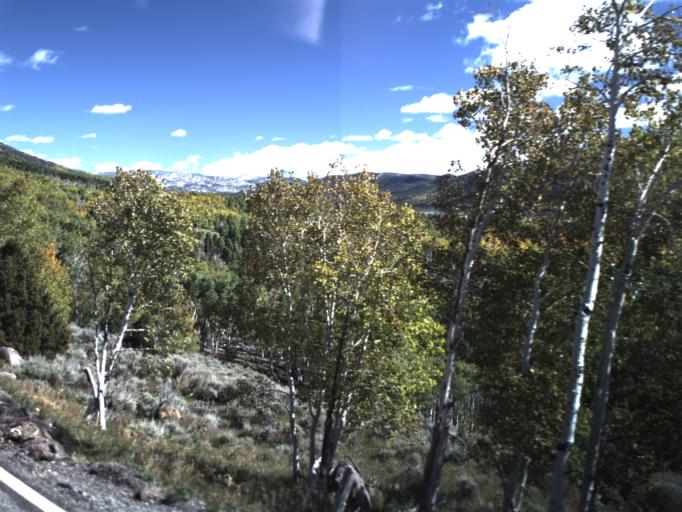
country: US
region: Utah
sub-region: Wayne County
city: Loa
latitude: 38.5181
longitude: -111.7576
